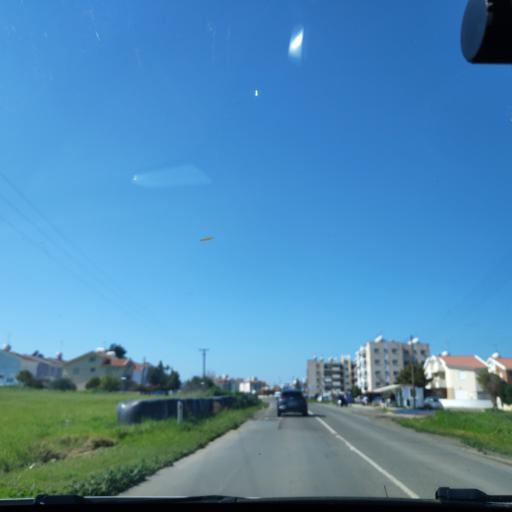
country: CY
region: Lefkosia
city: Tseri
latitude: 35.1127
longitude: 33.3263
